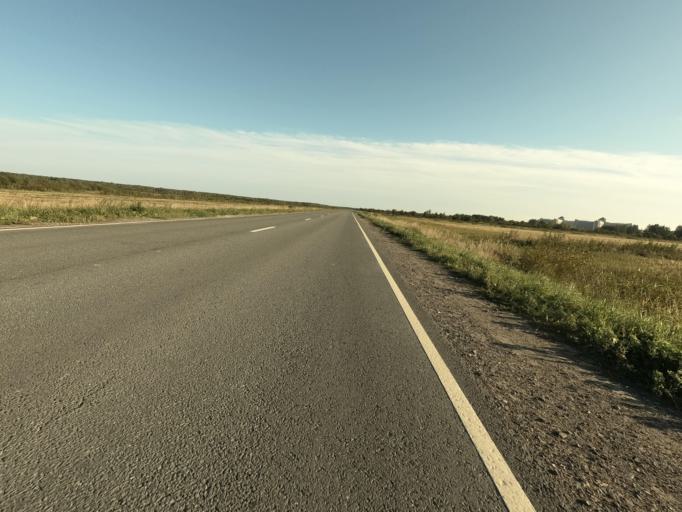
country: RU
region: St.-Petersburg
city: Sapernyy
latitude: 59.7529
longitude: 30.6348
